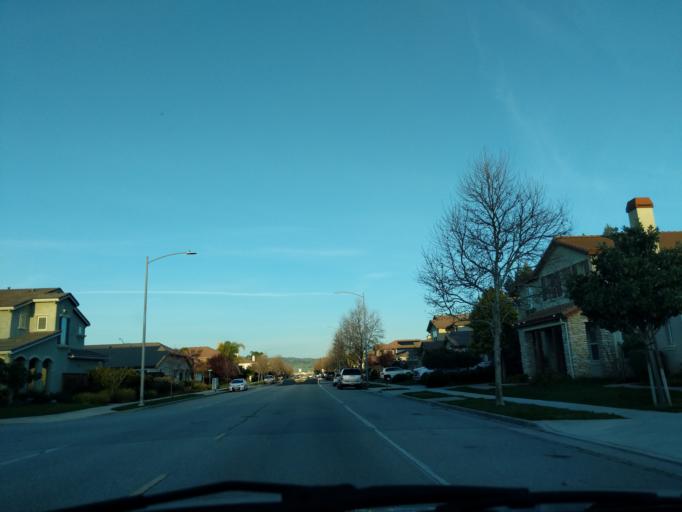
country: US
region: California
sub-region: Santa Clara County
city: Gilroy
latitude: 37.0331
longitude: -121.6071
